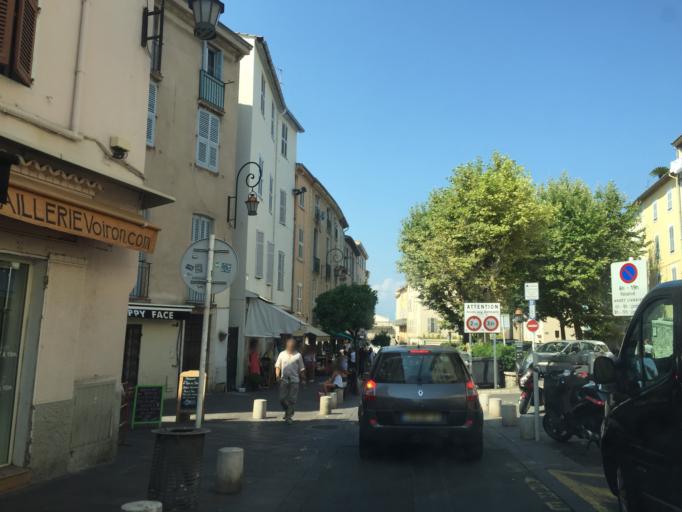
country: FR
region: Provence-Alpes-Cote d'Azur
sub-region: Departement des Alpes-Maritimes
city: Antibes
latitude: 43.5819
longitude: 7.1278
